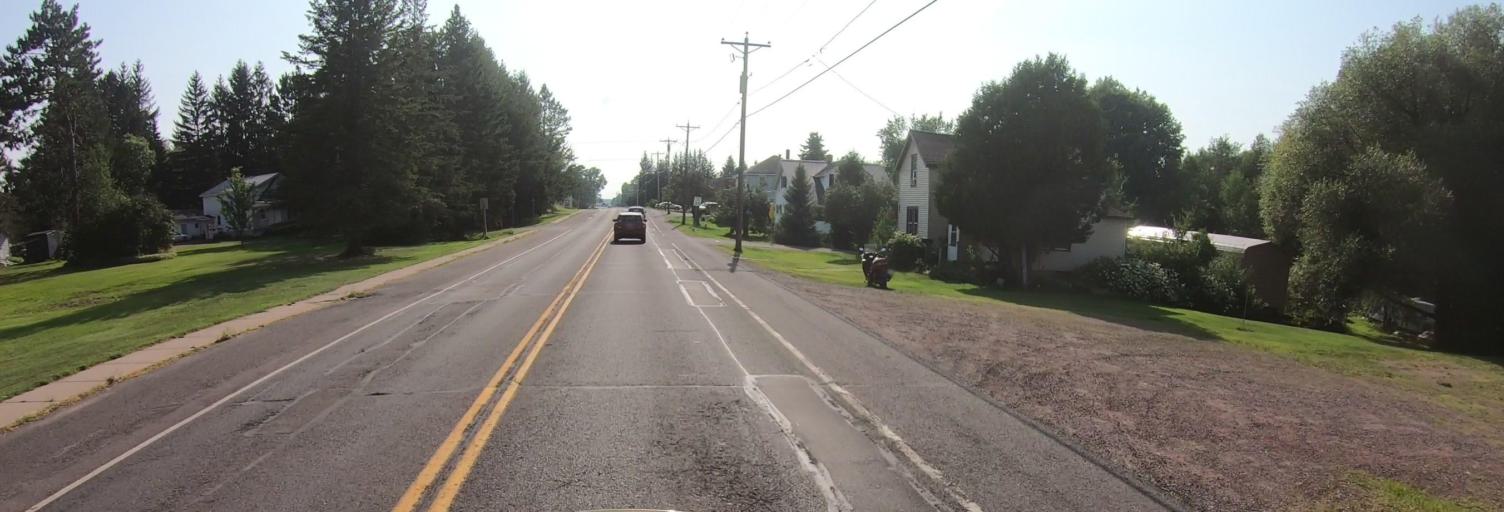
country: US
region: Wisconsin
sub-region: Iron County
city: Hurley
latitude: 46.4400
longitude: -90.2085
